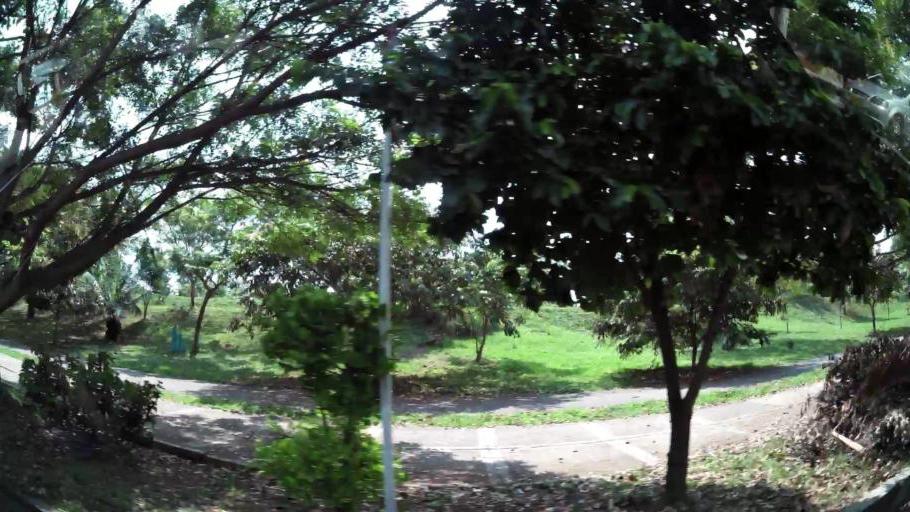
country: CO
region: Valle del Cauca
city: Cali
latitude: 3.4944
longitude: -76.4999
